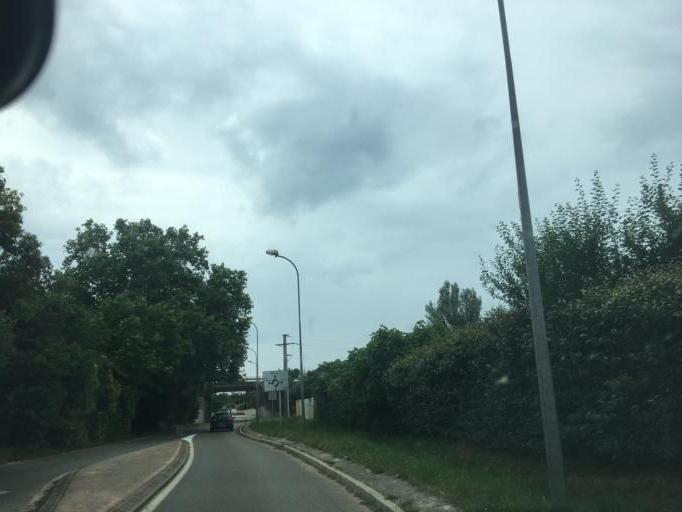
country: FR
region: Provence-Alpes-Cote d'Azur
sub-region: Departement du Var
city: La Londe-les-Maures
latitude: 43.1447
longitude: 6.2295
